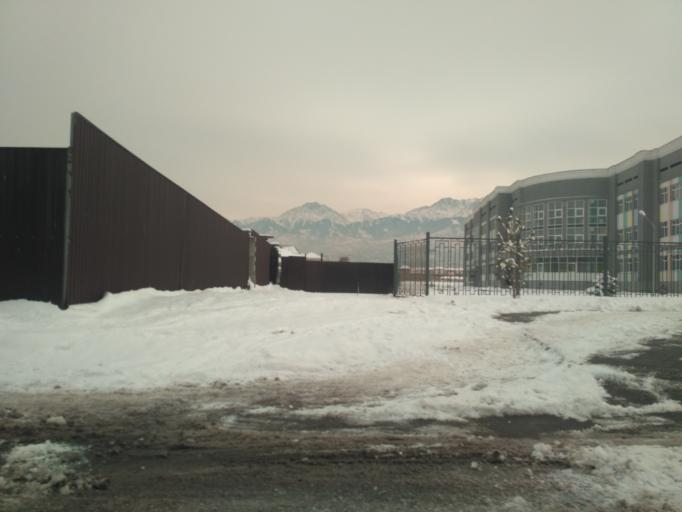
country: KZ
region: Almaty Qalasy
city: Almaty
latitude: 43.2164
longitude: 76.7922
